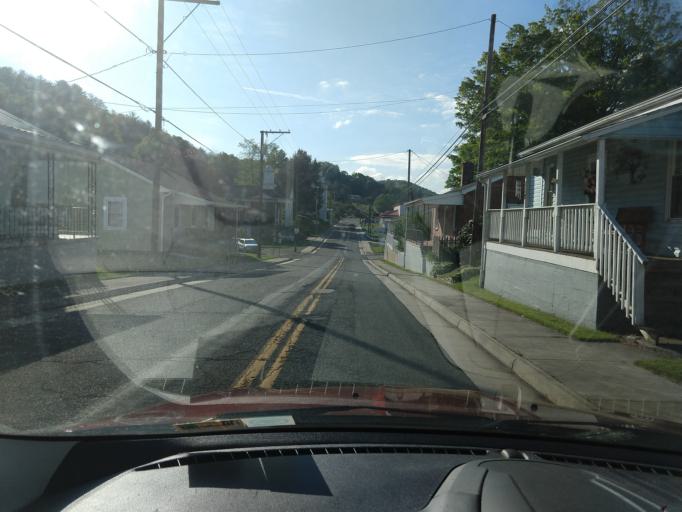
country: US
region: Virginia
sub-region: City of Galax
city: Galax
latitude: 36.7154
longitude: -80.9746
